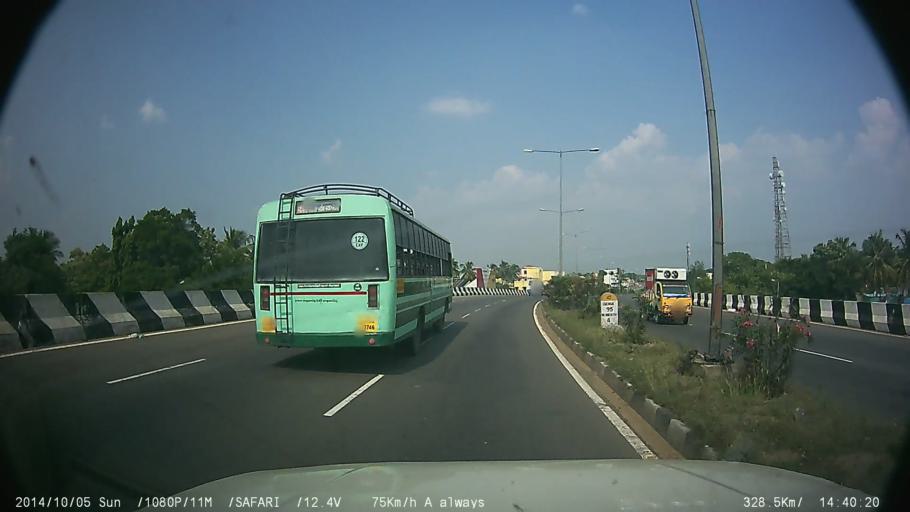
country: IN
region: Tamil Nadu
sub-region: Kancheepuram
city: Madurantakam
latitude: 12.4063
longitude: 79.8144
